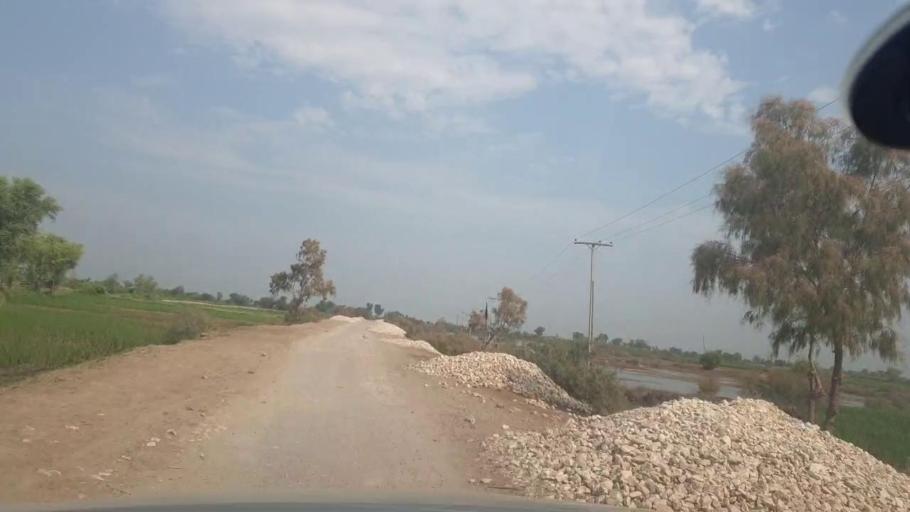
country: PK
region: Balochistan
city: Mehrabpur
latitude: 28.0681
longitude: 68.1029
